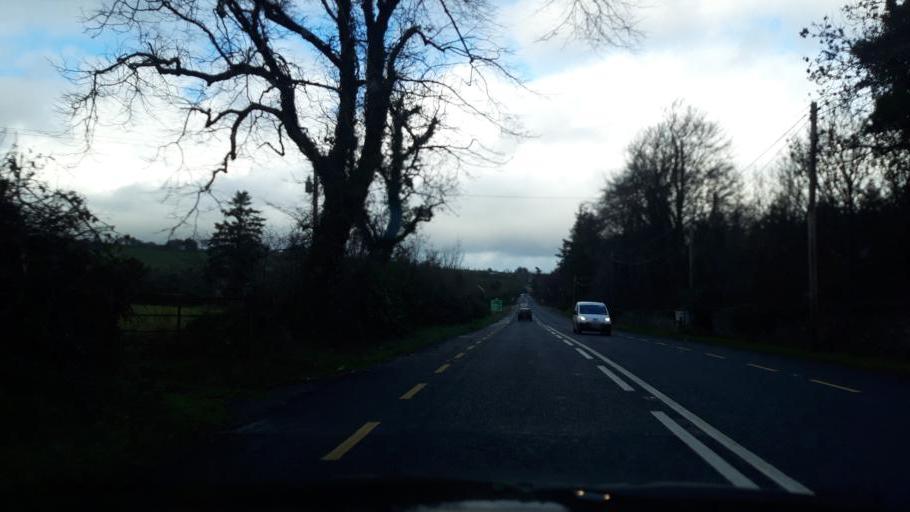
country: IE
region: Leinster
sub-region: Lu
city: Tullyallen
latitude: 53.7857
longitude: -6.4887
